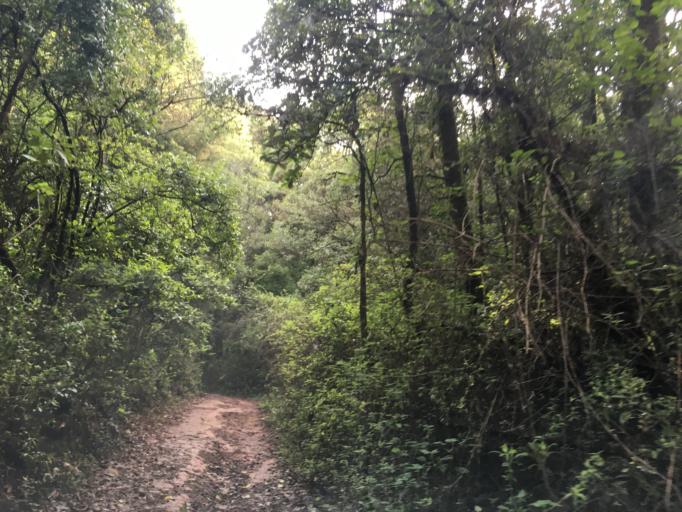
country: MX
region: Michoacan
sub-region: Zitacuaro
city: Francisco Serrato (San Bartolo)
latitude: 19.5139
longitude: -100.3026
